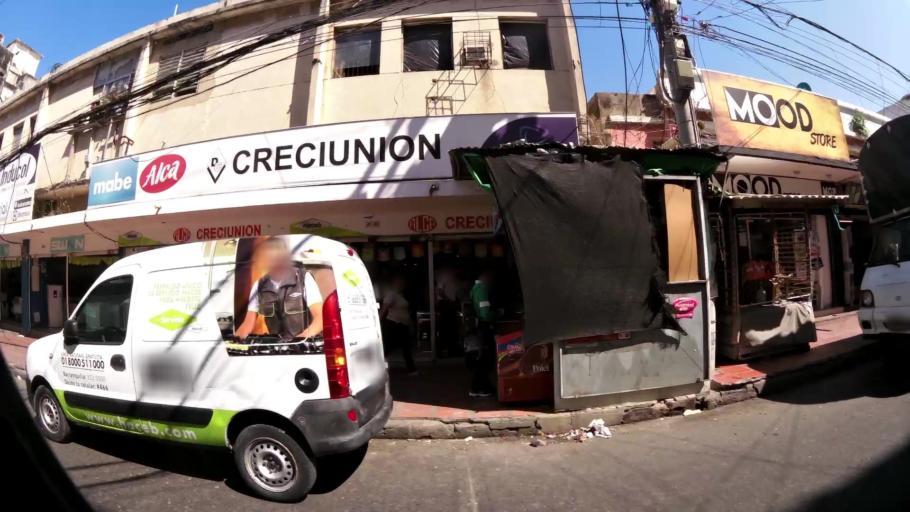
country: CO
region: Atlantico
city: Barranquilla
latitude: 10.9810
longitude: -74.7809
